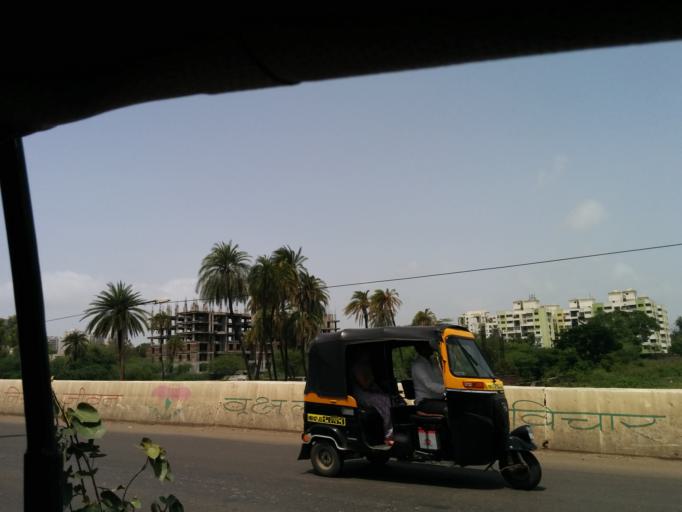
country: IN
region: Maharashtra
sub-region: Pune Division
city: Lohogaon
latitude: 18.5287
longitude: 73.9324
